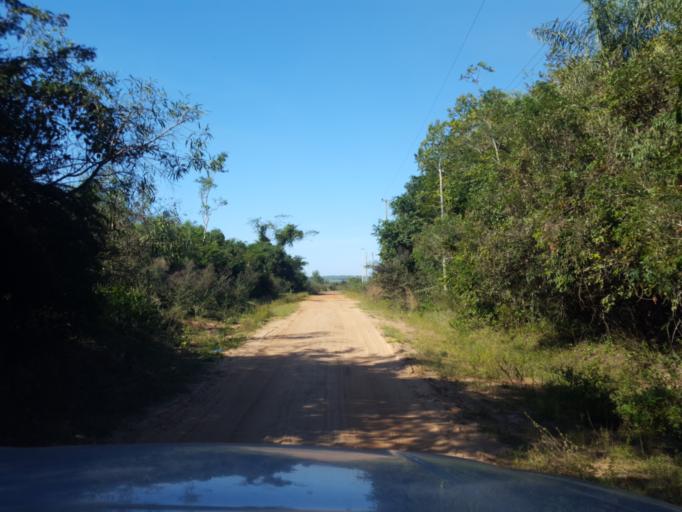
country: PY
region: Cordillera
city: Atyra
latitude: -25.2452
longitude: -57.1313
